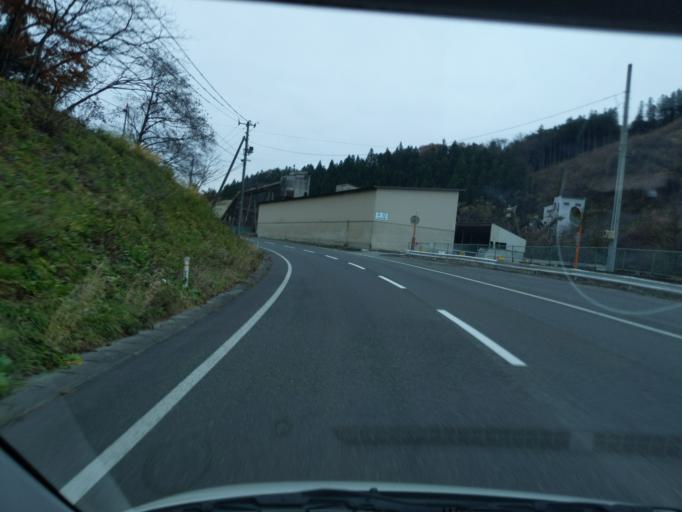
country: JP
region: Iwate
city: Kitakami
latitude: 39.2287
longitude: 141.2710
